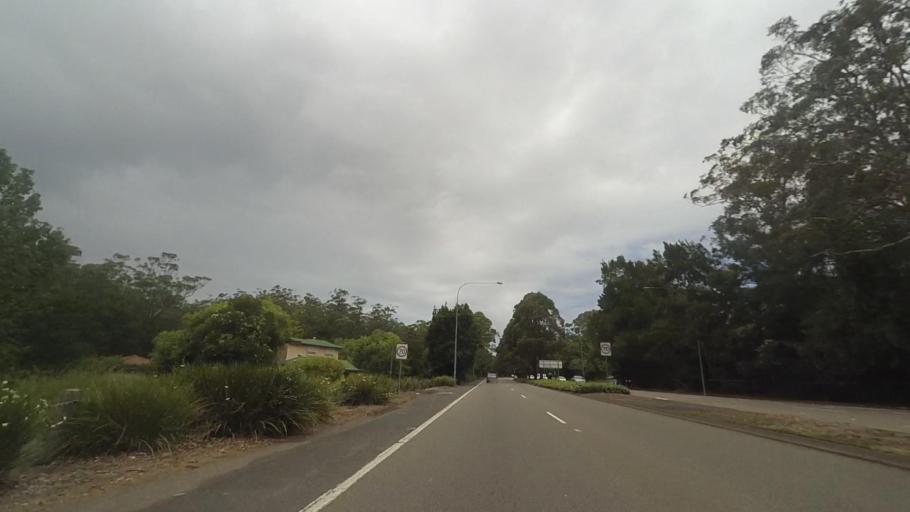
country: AU
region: New South Wales
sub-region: Wyong Shire
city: Berkeley Vale
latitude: -33.3426
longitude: 151.4289
